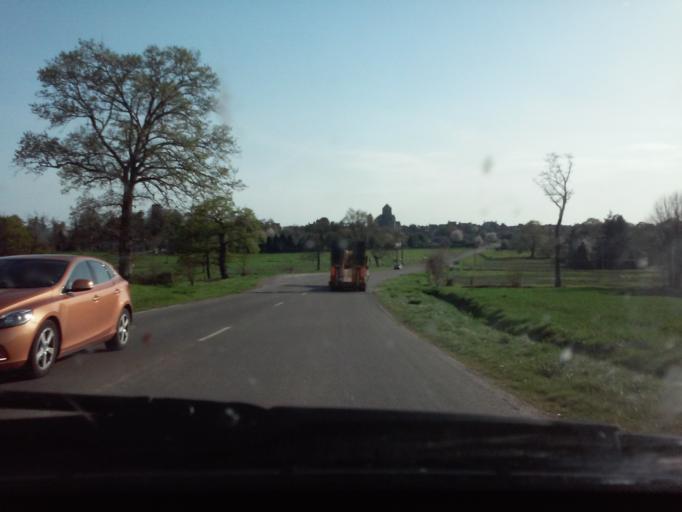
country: FR
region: Brittany
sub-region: Departement d'Ille-et-Vilaine
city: Saint-Aubin-du-Cormier
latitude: 48.2675
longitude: -1.3932
